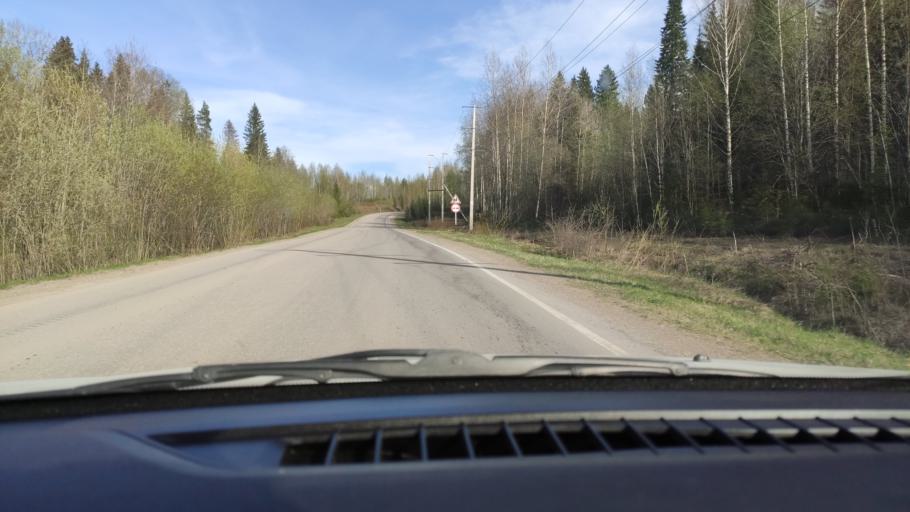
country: RU
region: Perm
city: Novyye Lyady
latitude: 57.9294
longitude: 56.6483
